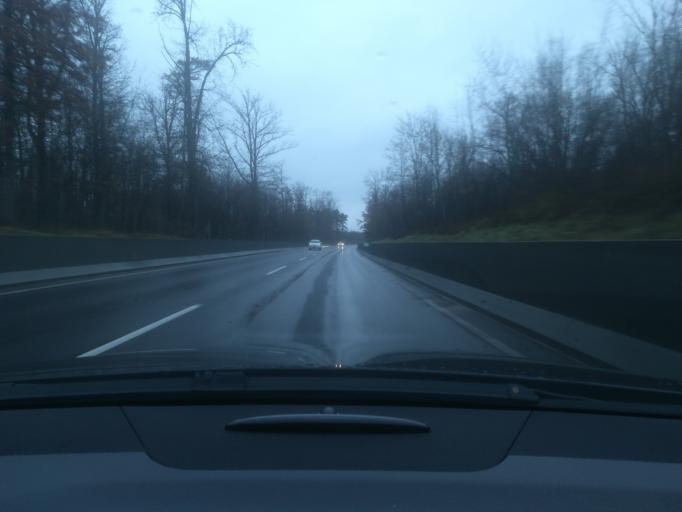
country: AT
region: Upper Austria
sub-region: Politischer Bezirk Linz-Land
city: Traun
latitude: 48.2345
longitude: 14.2217
